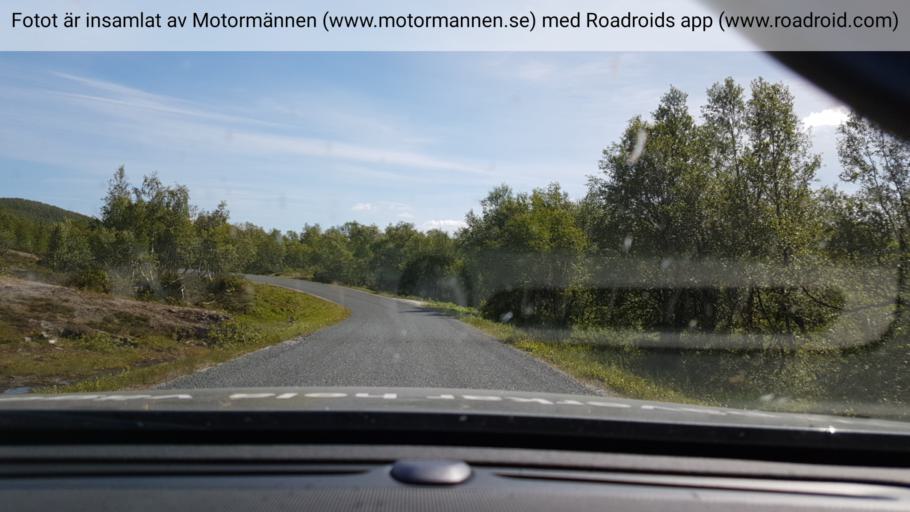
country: NO
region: Nordland
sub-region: Hattfjelldal
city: Hattfjelldal
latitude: 65.4162
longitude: 14.6900
